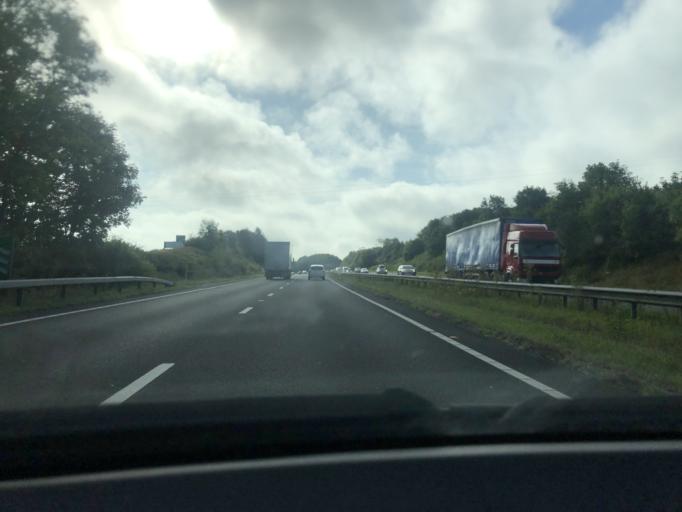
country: GB
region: England
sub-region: Devon
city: Crediton
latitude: 50.7293
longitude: -3.7329
